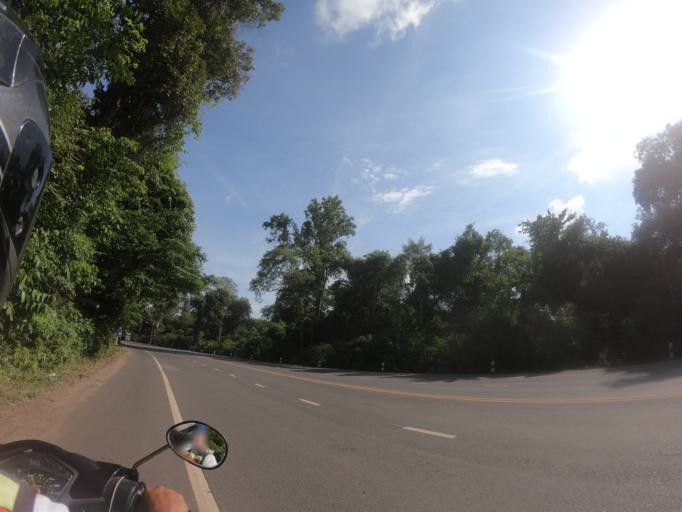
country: TH
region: Surin
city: Kap Choeng
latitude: 14.4487
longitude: 103.7004
